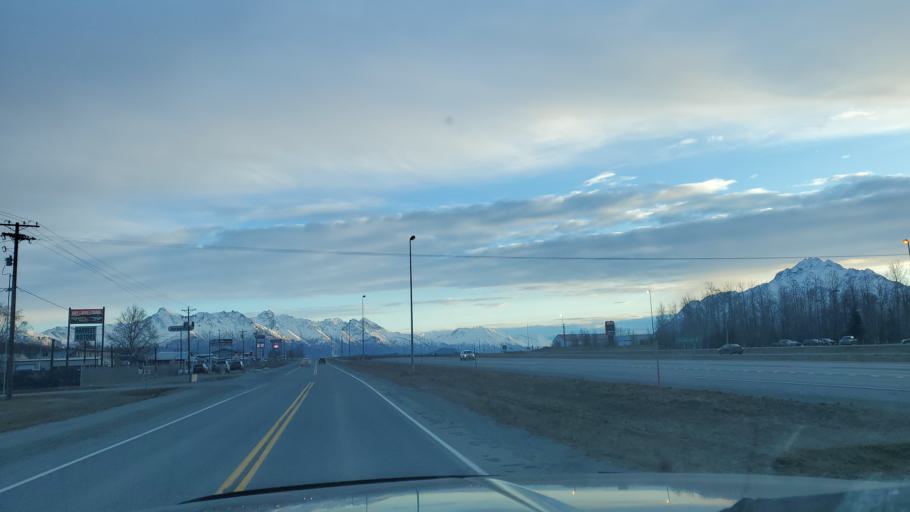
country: US
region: Alaska
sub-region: Matanuska-Susitna Borough
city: Gateway
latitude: 61.5632
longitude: -149.2780
